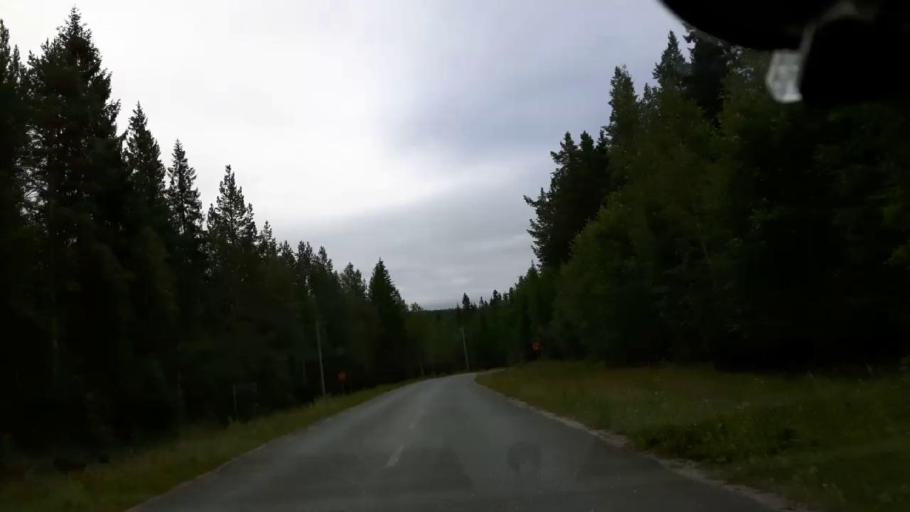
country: SE
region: Jaemtland
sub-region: Braecke Kommun
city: Braecke
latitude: 62.8874
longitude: 15.6175
